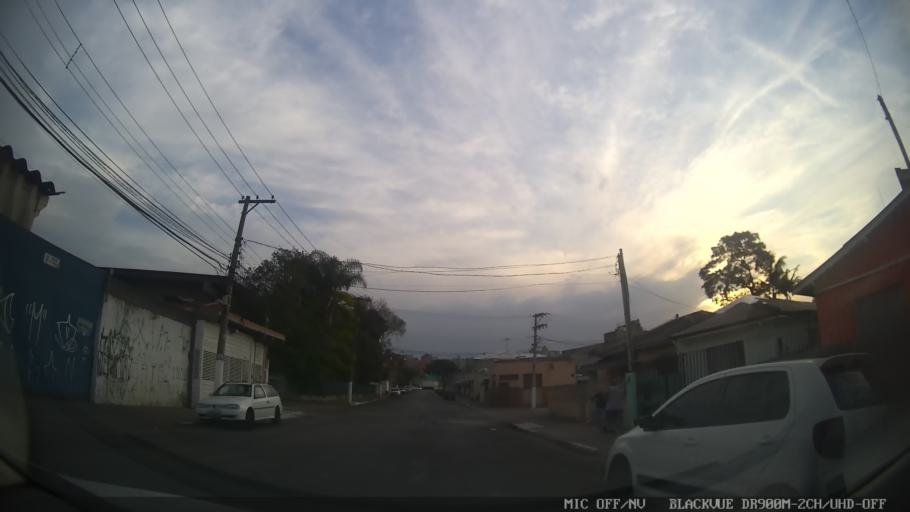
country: BR
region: Sao Paulo
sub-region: Sao Caetano Do Sul
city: Sao Caetano do Sul
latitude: -23.6014
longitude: -46.5909
